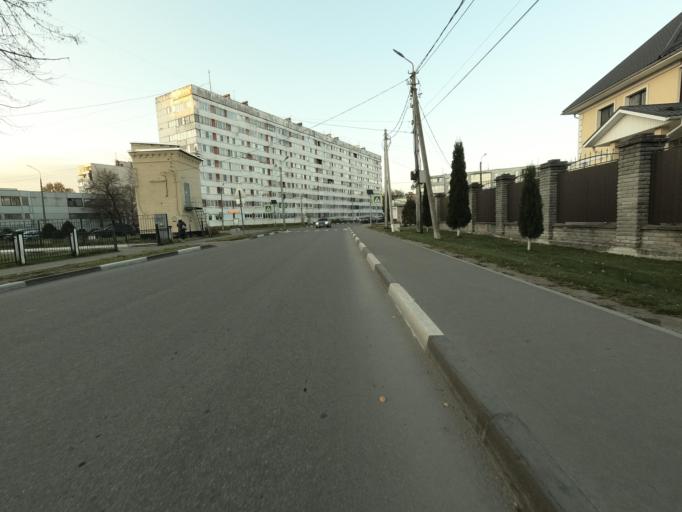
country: RU
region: Leningrad
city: Kirovsk
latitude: 59.8793
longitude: 30.9905
